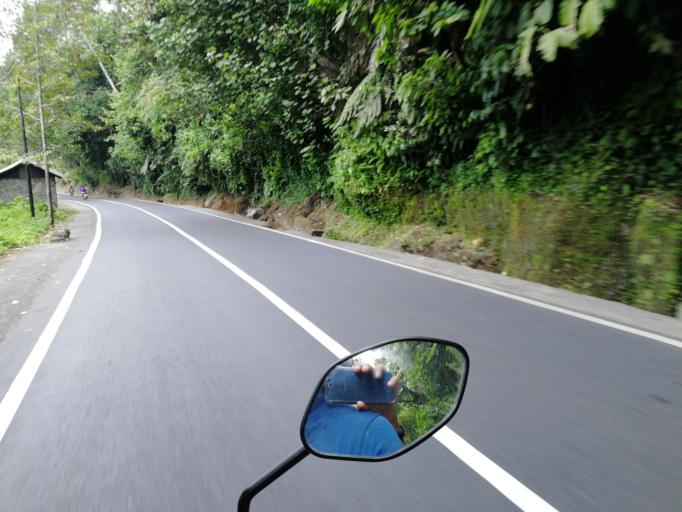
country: ID
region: Bali
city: Banjar Geriana Kangin
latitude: -8.4256
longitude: 115.4393
